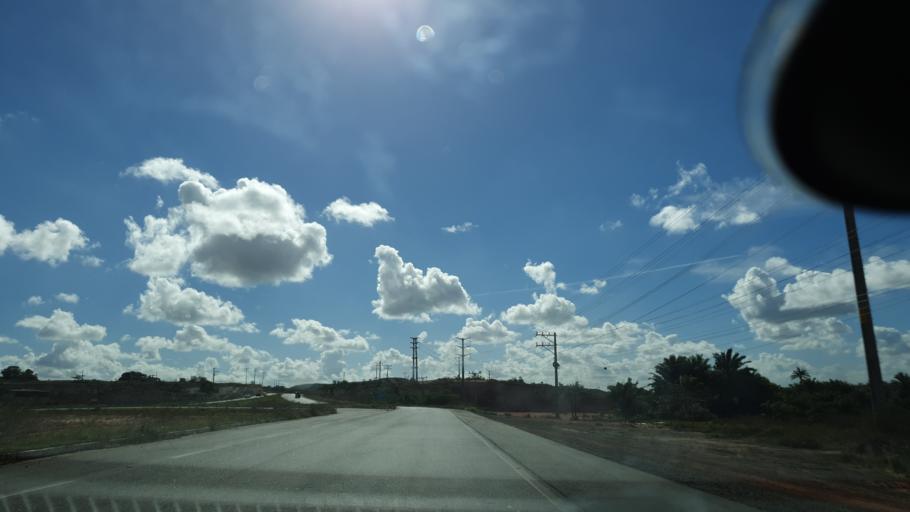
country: BR
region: Bahia
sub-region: Camacari
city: Camacari
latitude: -12.6832
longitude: -38.2477
